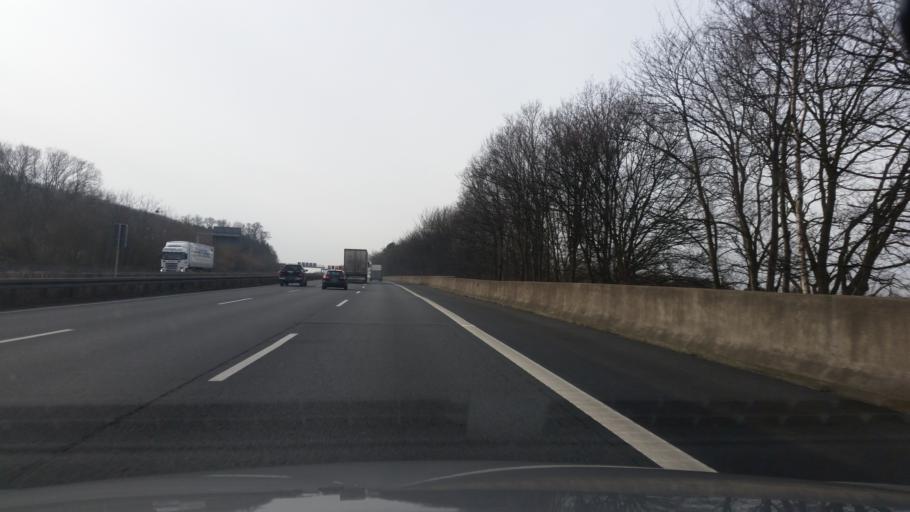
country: DE
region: Lower Saxony
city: Bad Nenndorf
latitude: 52.3260
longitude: 9.3940
